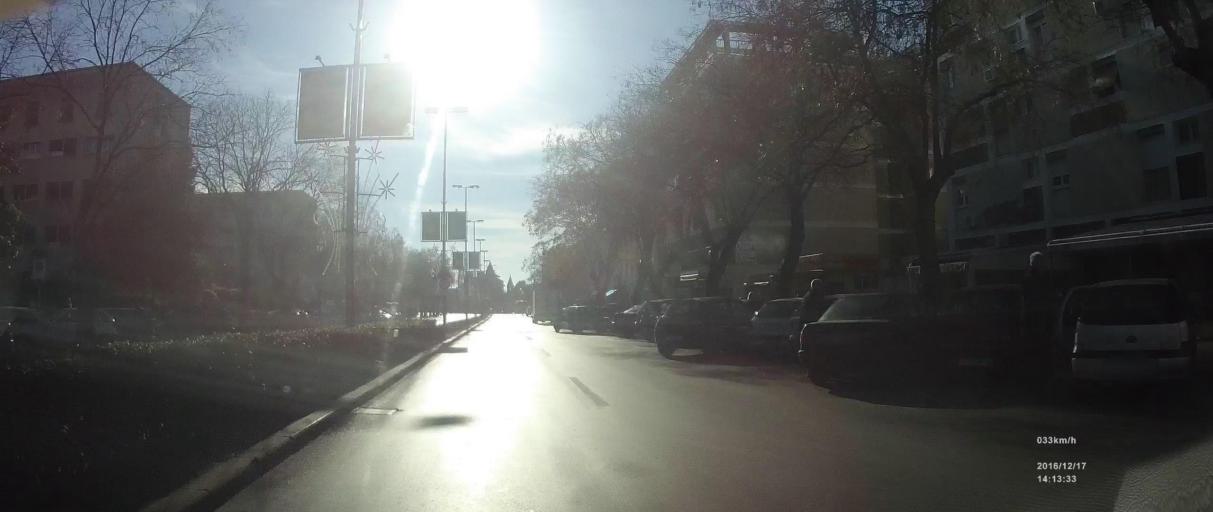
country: HR
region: Splitsko-Dalmatinska
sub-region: Grad Split
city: Split
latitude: 43.5141
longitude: 16.4433
